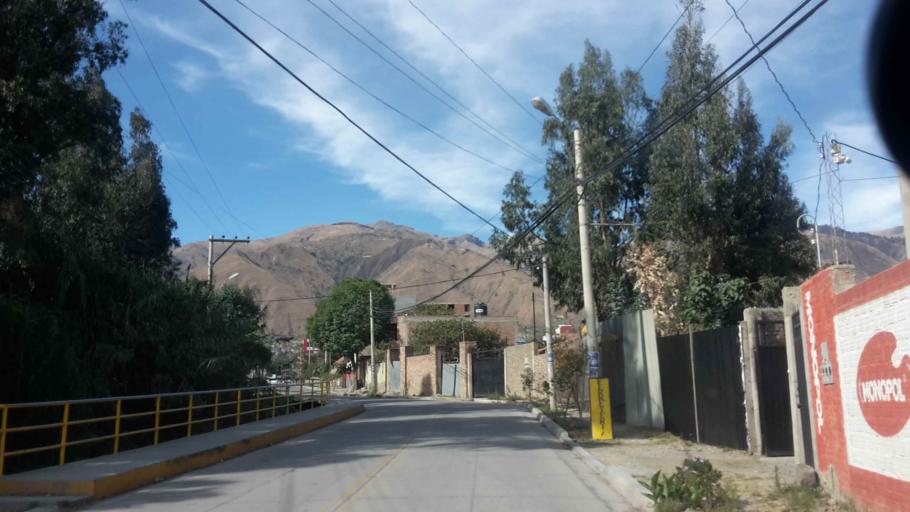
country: BO
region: Cochabamba
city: Cochabamba
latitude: -17.3484
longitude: -66.2052
